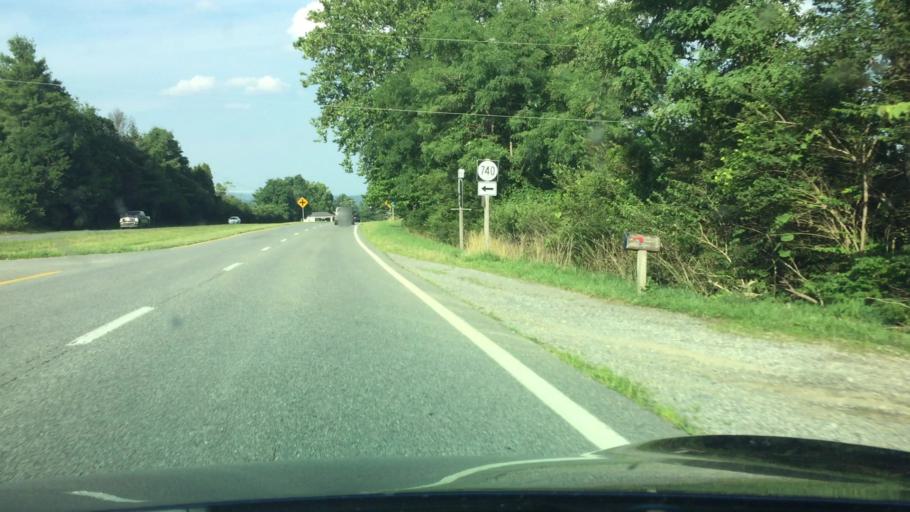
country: US
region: Virginia
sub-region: Pulaski County
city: Fairlawn
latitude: 37.1467
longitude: -80.5984
